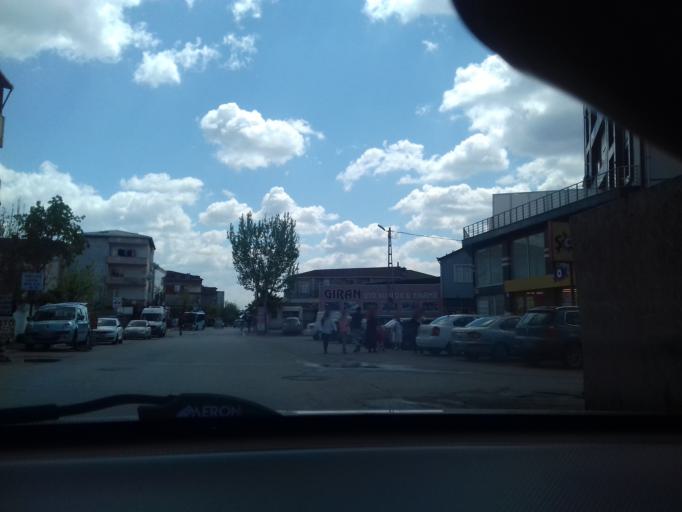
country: TR
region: Istanbul
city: Pendik
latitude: 40.8900
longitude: 29.2788
